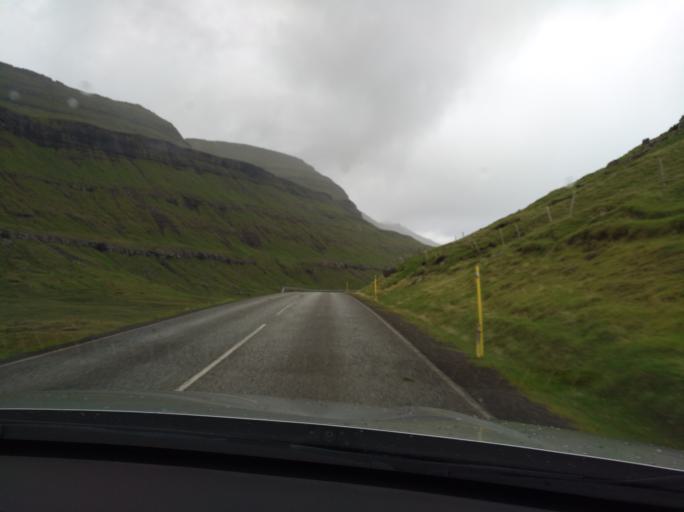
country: FO
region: Eysturoy
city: Fuglafjordur
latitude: 62.2312
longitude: -6.8800
